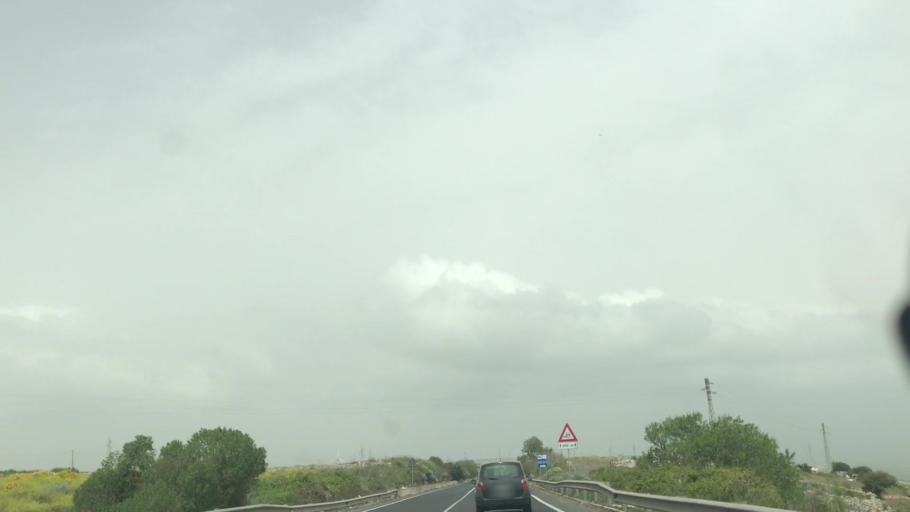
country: IT
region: Sicily
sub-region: Ragusa
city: Ragusa
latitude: 36.8749
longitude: 14.6918
